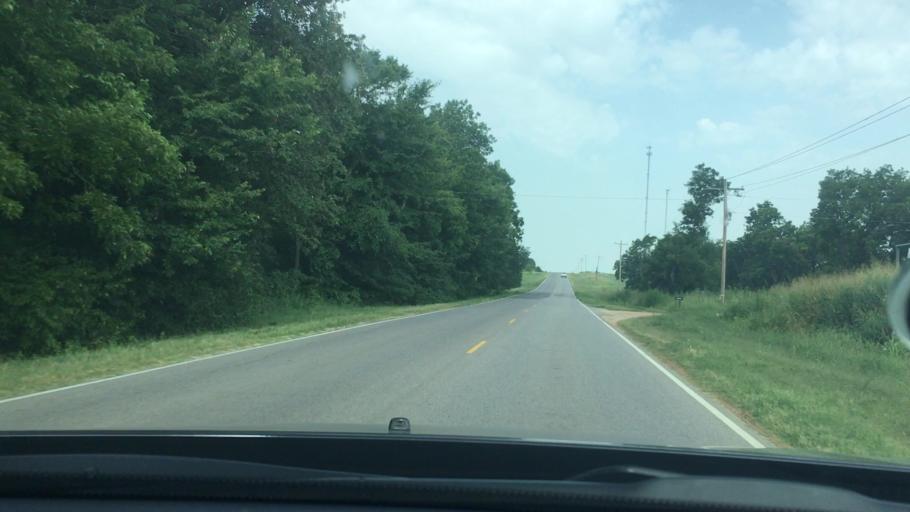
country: US
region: Oklahoma
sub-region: Garvin County
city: Stratford
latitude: 34.7967
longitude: -96.8744
